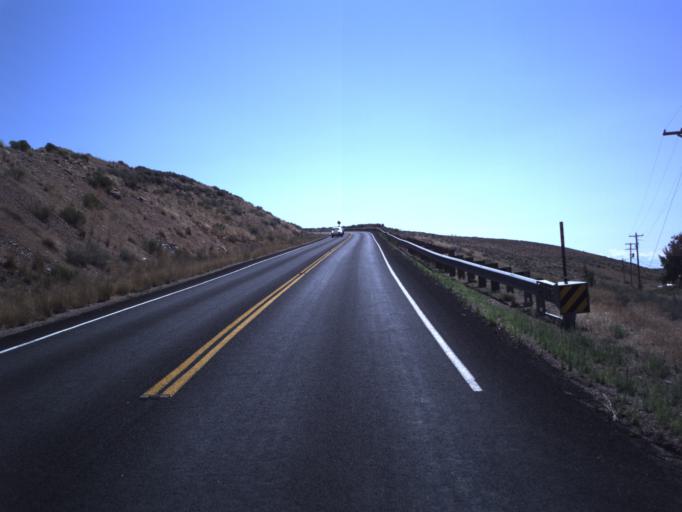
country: US
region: Utah
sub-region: Uintah County
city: Maeser
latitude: 40.4033
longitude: -109.7744
